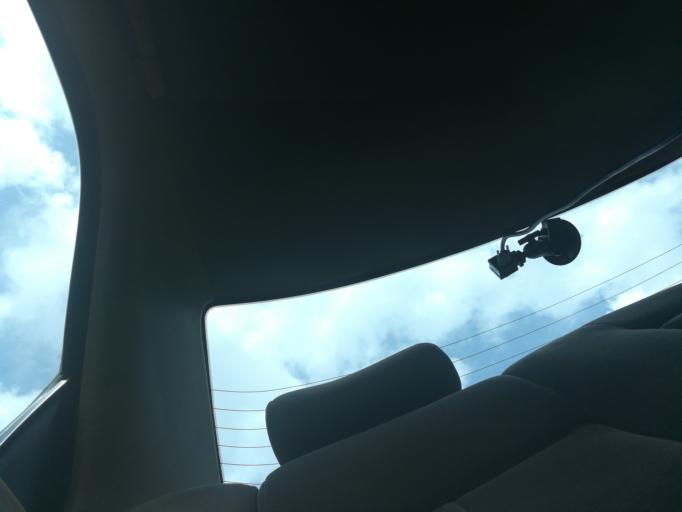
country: NG
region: Lagos
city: Ikorodu
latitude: 6.6635
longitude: 3.6117
